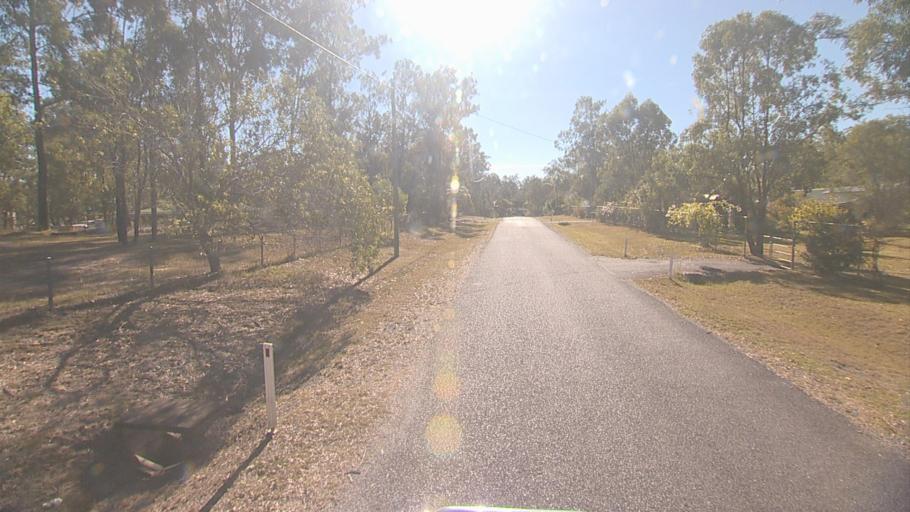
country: AU
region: Queensland
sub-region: Logan
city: North Maclean
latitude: -27.8093
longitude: 152.9667
